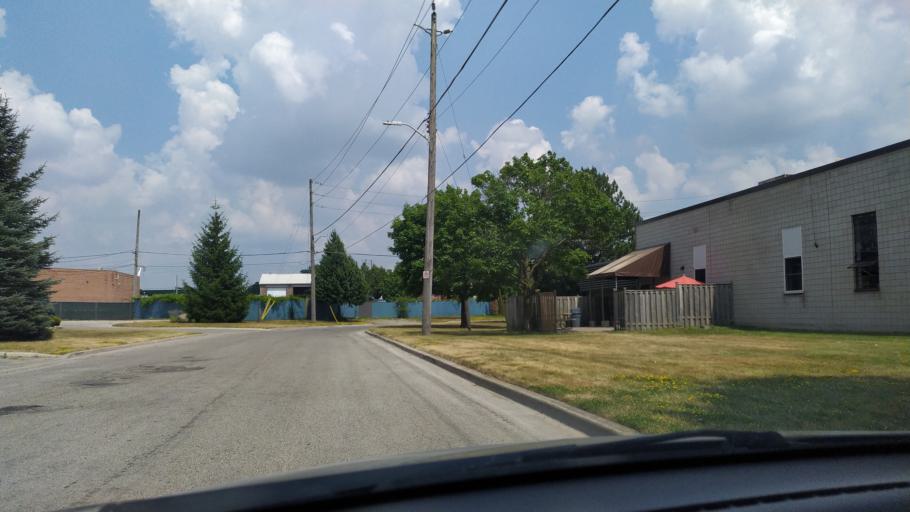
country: CA
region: Ontario
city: London
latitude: 42.9876
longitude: -81.1699
